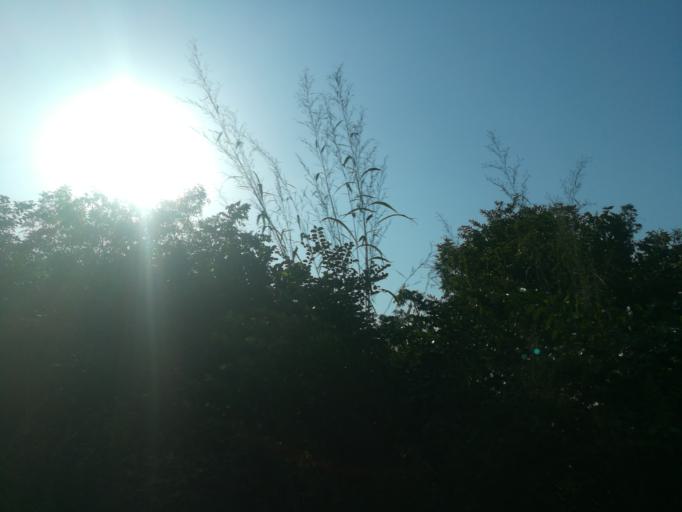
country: NG
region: Ogun
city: Abeokuta
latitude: 7.2463
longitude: 3.3006
